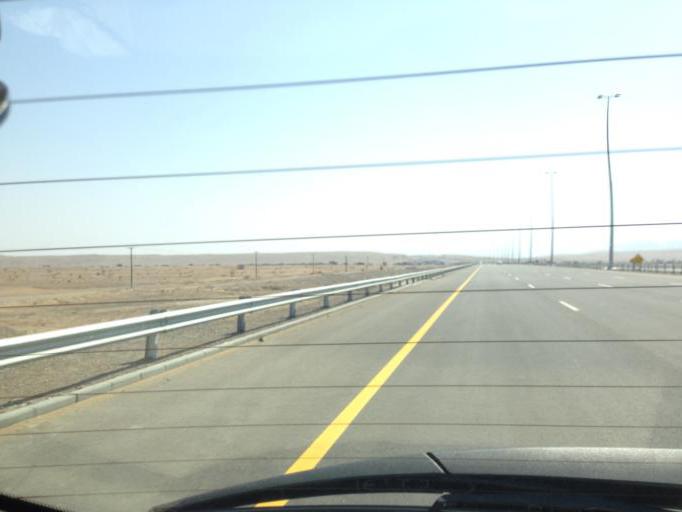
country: OM
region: Al Batinah
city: Rustaq
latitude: 23.5236
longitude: 57.6098
